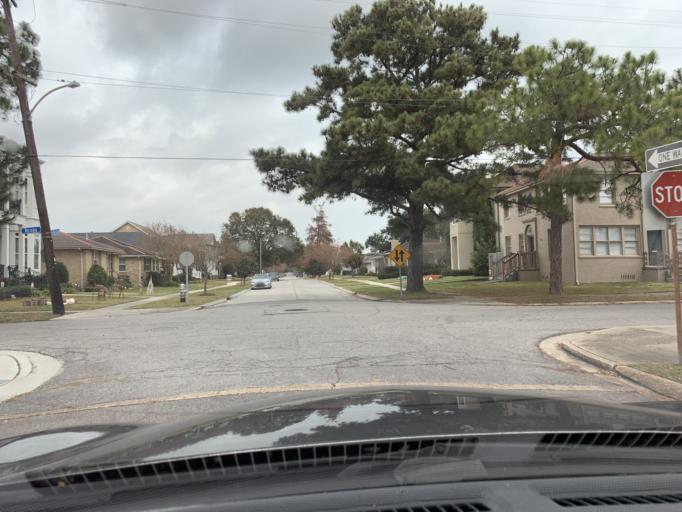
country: US
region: Louisiana
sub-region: Jefferson Parish
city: Metairie
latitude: 30.0063
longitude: -90.1036
